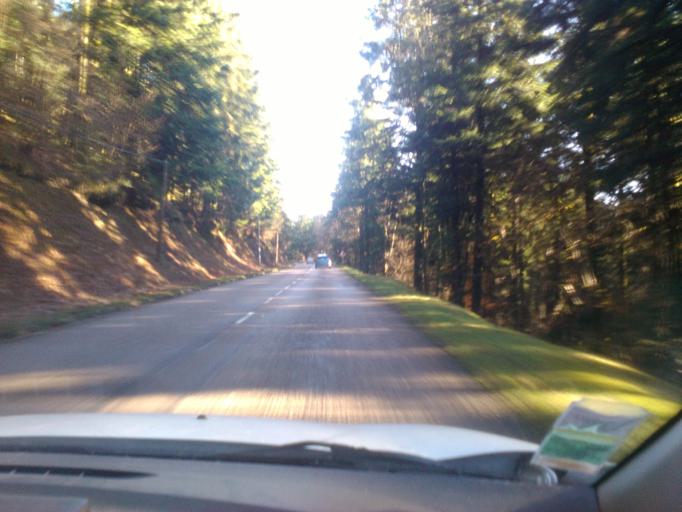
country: FR
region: Lorraine
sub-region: Departement des Vosges
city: Remiremont
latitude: 47.9688
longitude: 6.5333
